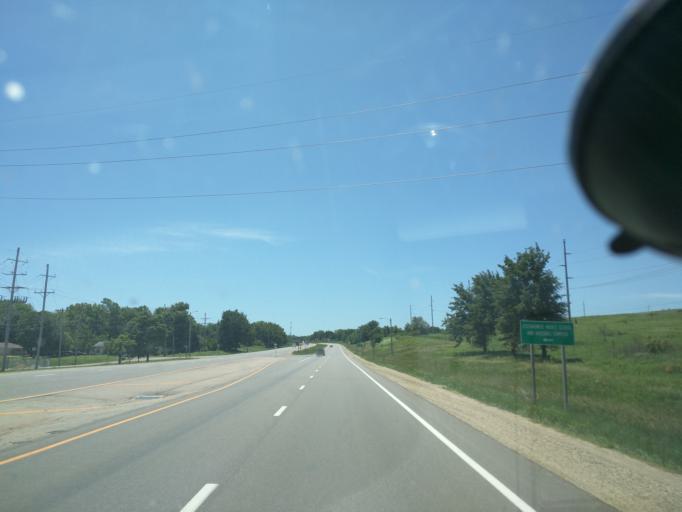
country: US
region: Kansas
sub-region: Riley County
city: Manhattan
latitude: 39.2172
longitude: -96.5782
